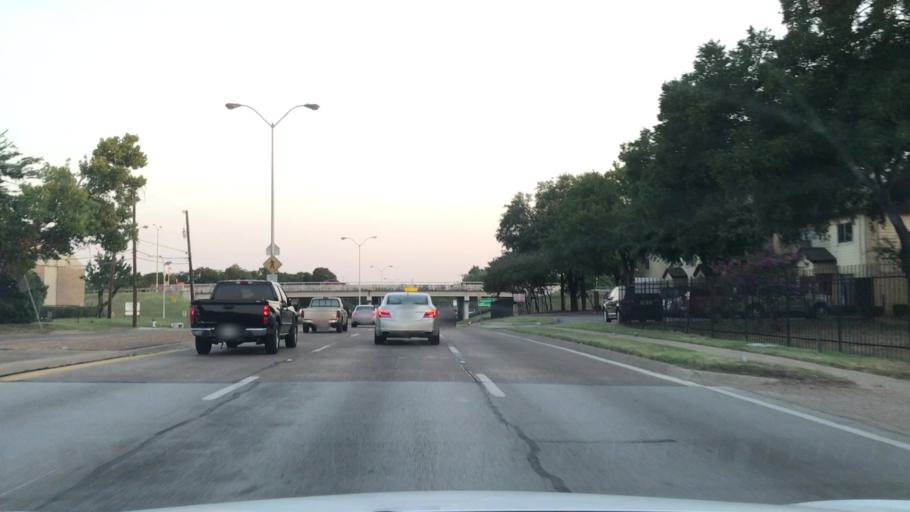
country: US
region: Texas
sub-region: Dallas County
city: Mesquite
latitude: 32.8162
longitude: -96.6887
